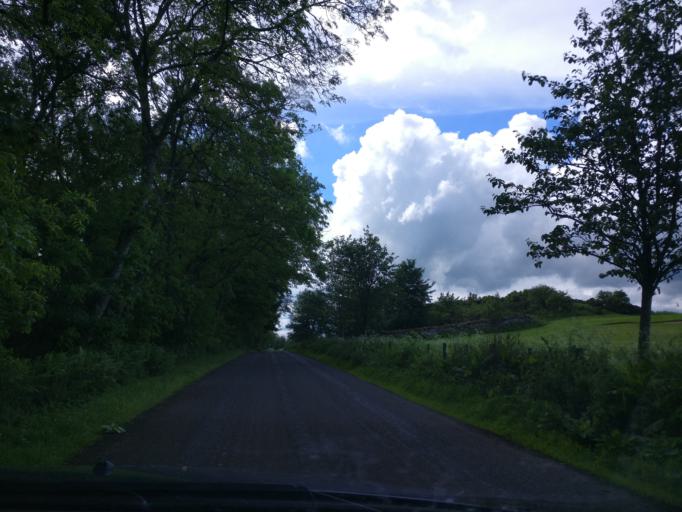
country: GB
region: Scotland
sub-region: East Lothian
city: Haddington
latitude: 55.8844
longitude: -2.7262
